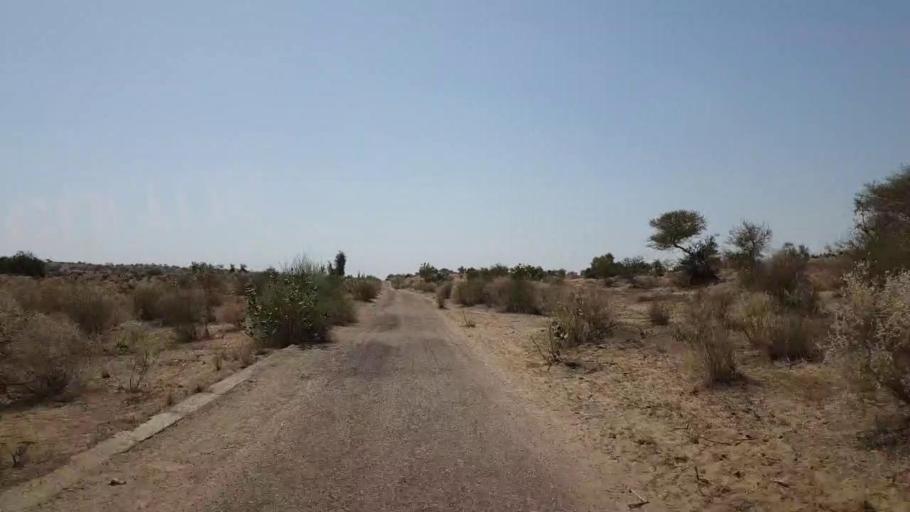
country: PK
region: Sindh
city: Umarkot
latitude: 25.1803
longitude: 69.8778
